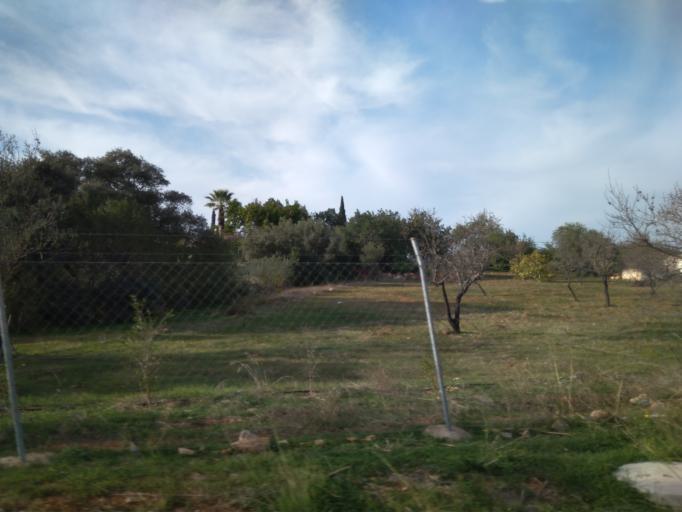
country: PT
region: Faro
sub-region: Faro
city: Santa Barbara de Nexe
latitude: 37.0925
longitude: -7.9080
